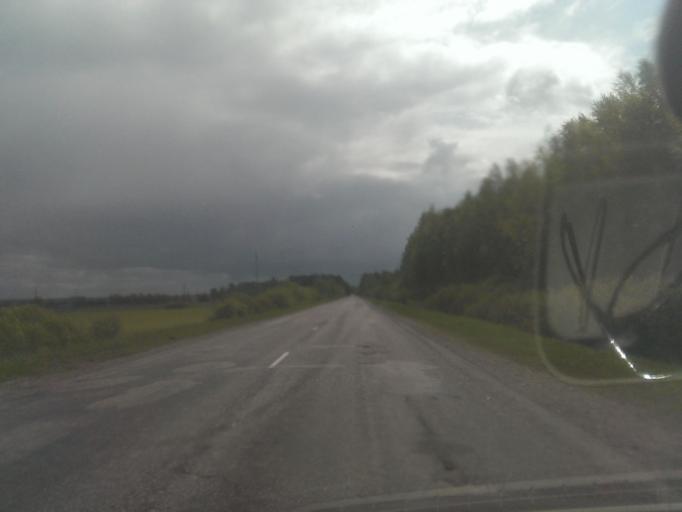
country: LV
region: Ventspils Rajons
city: Piltene
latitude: 57.1889
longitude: 21.6403
